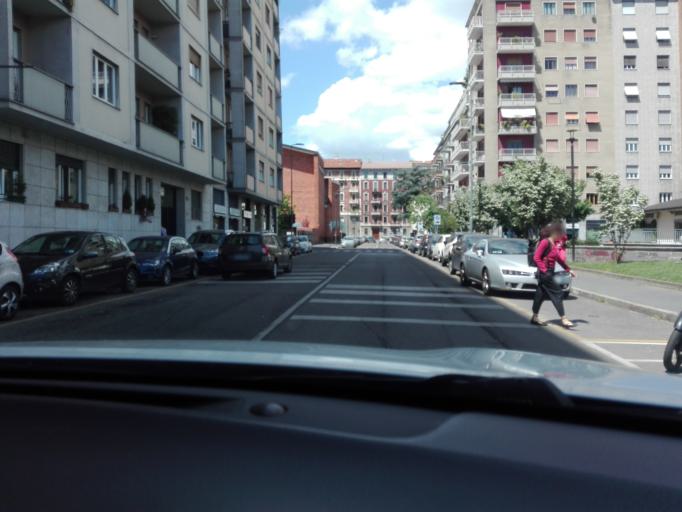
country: IT
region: Lombardy
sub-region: Citta metropolitana di Milano
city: Milano
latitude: 45.4617
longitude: 9.1572
